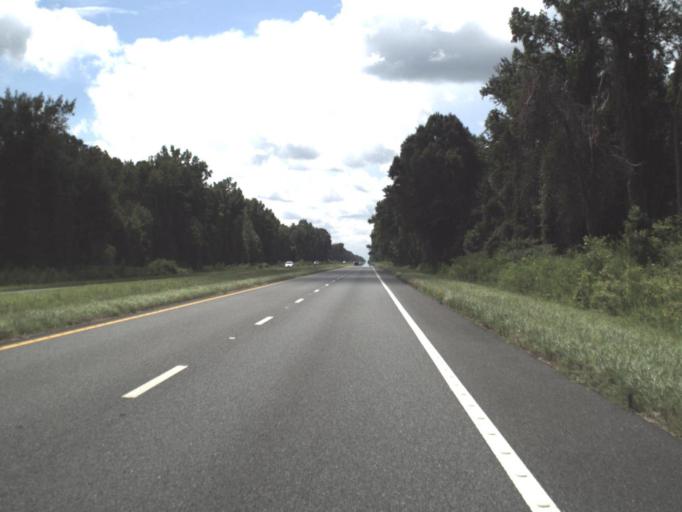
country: US
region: Florida
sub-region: Taylor County
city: Perry
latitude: 30.2894
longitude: -83.7357
